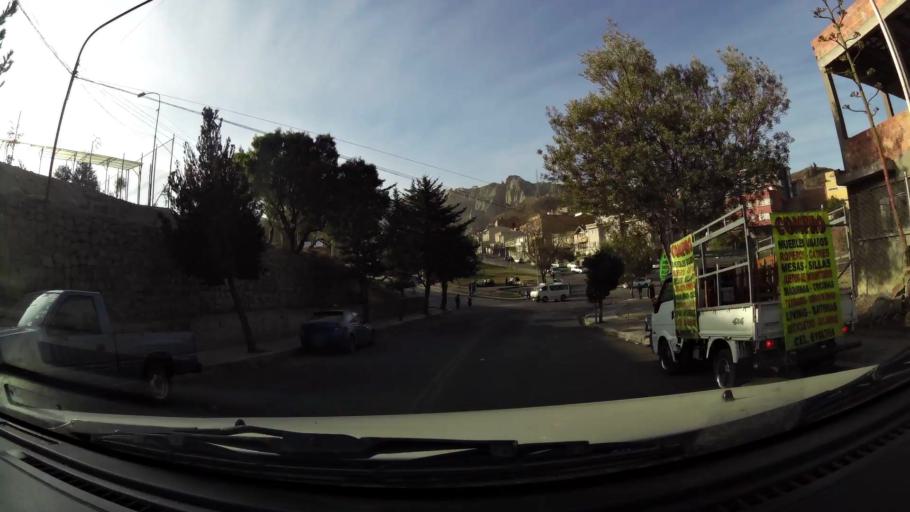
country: BO
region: La Paz
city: La Paz
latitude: -16.5223
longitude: -68.1041
